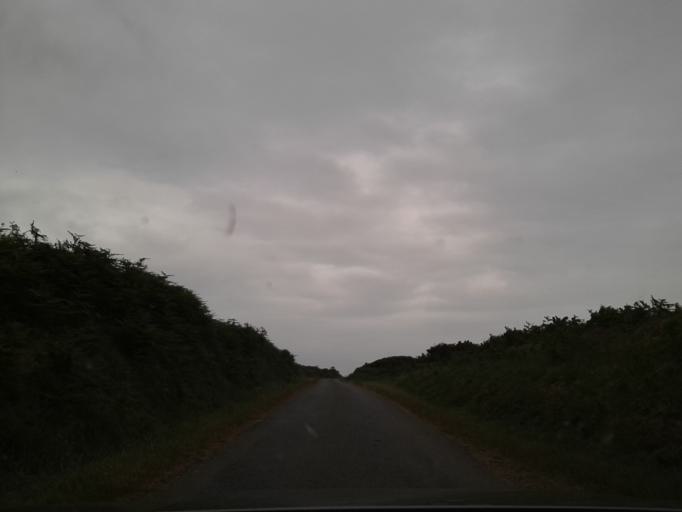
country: FR
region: Lower Normandy
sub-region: Departement de la Manche
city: Beaumont-Hague
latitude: 49.6952
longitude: -1.9173
